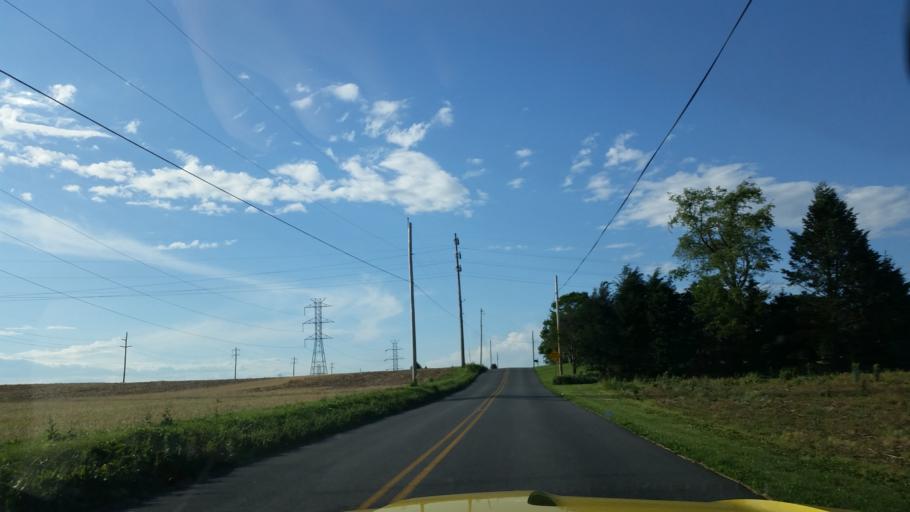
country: US
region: Pennsylvania
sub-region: Lebanon County
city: Avon
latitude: 40.3390
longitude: -76.3625
